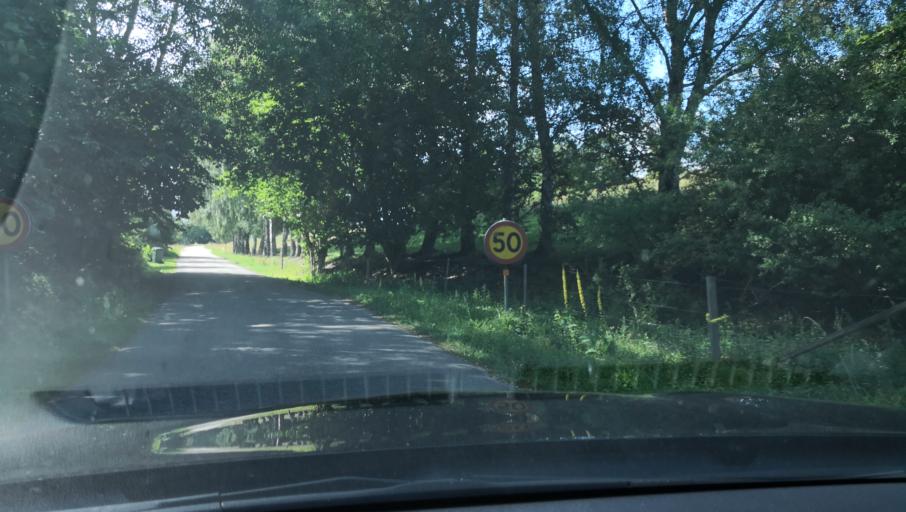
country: SE
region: Skane
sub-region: Ystads Kommun
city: Kopingebro
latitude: 55.3873
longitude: 14.1463
